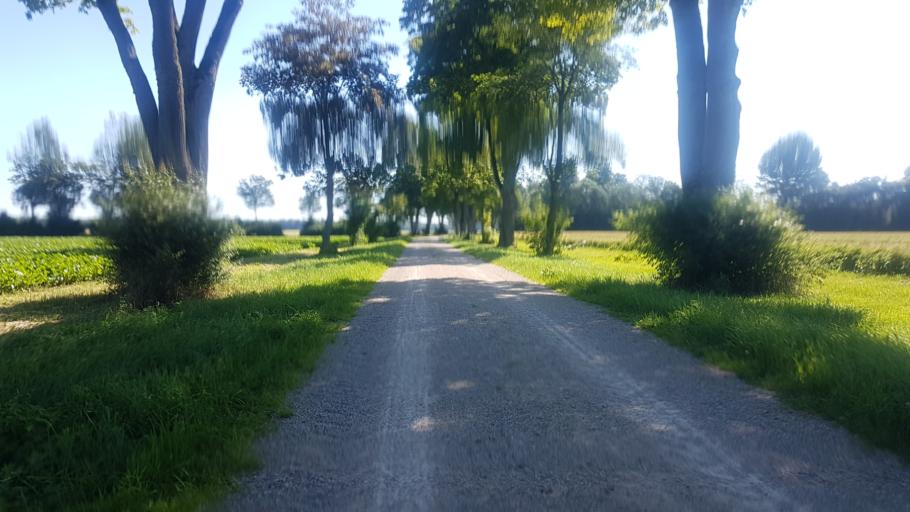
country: DE
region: Bavaria
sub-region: Upper Bavaria
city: Weichering
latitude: 48.7263
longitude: 11.2827
